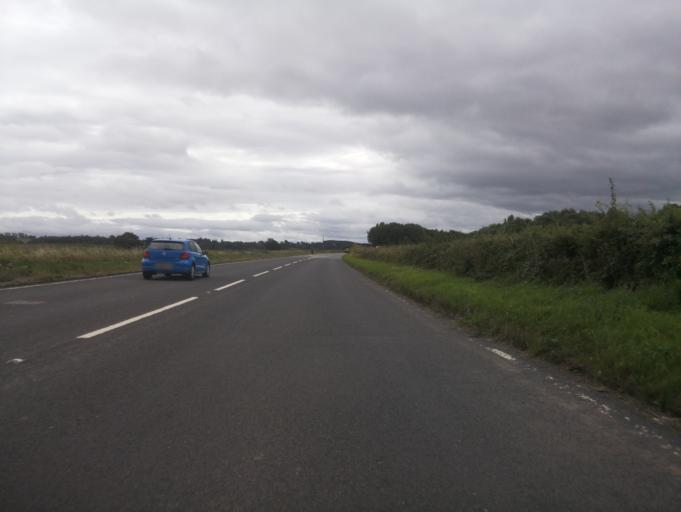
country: GB
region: England
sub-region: Worcestershire
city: Kempsey
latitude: 52.1103
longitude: -2.2199
